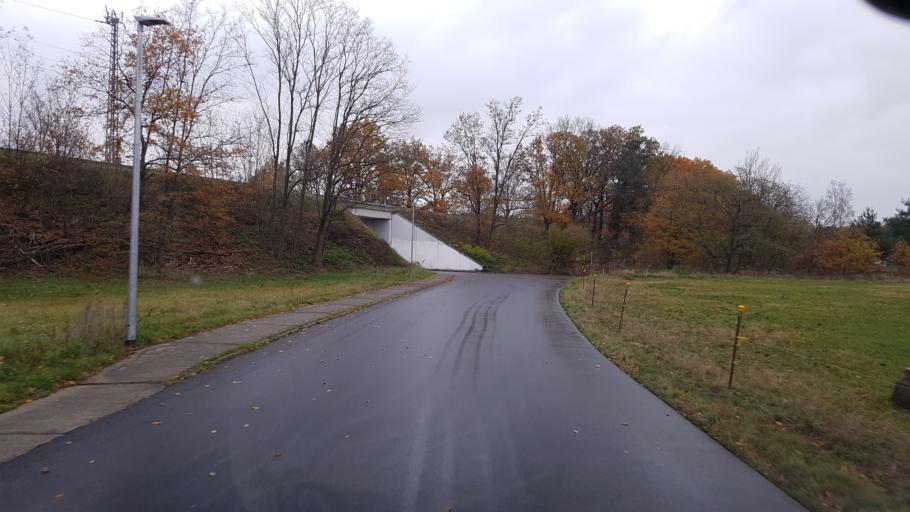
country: DE
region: Brandenburg
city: Ortrand
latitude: 51.3777
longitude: 13.7695
